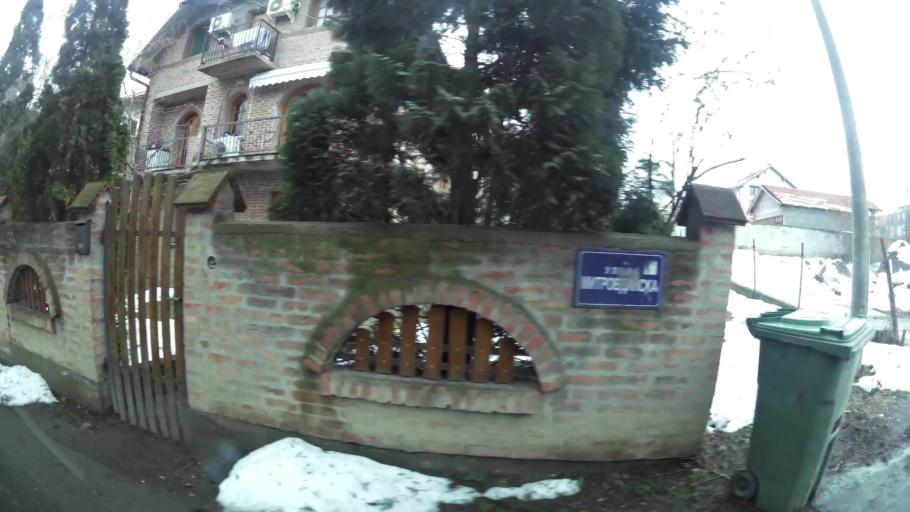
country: RS
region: Central Serbia
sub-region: Belgrade
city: Vozdovac
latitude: 44.7611
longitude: 20.4977
